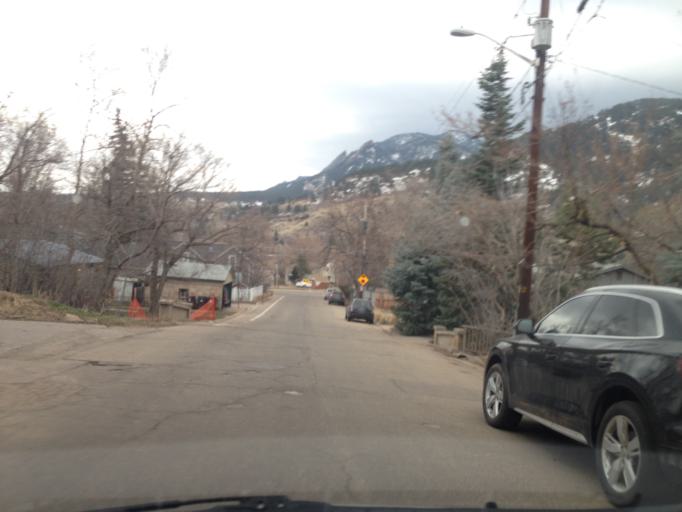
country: US
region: Colorado
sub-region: Boulder County
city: Boulder
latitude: 40.0177
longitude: -105.2915
